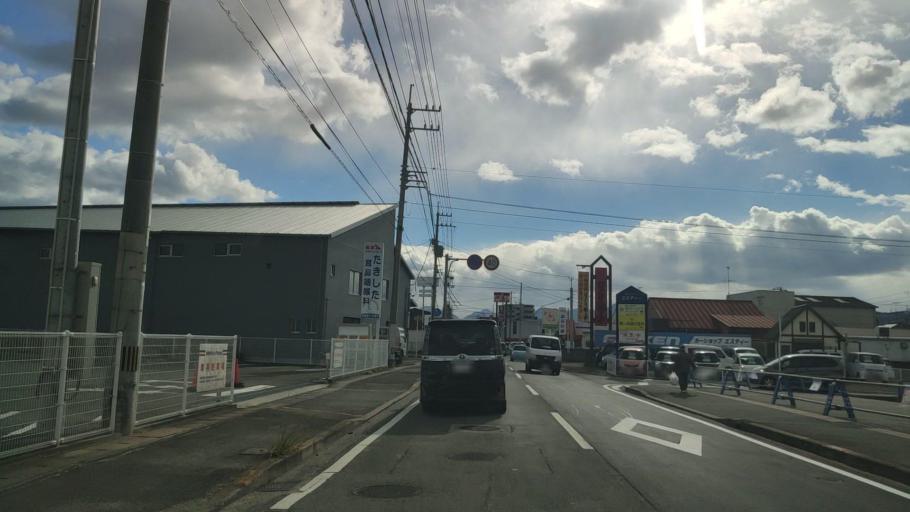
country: JP
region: Ehime
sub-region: Shikoku-chuo Shi
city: Matsuyama
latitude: 33.8118
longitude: 132.7953
